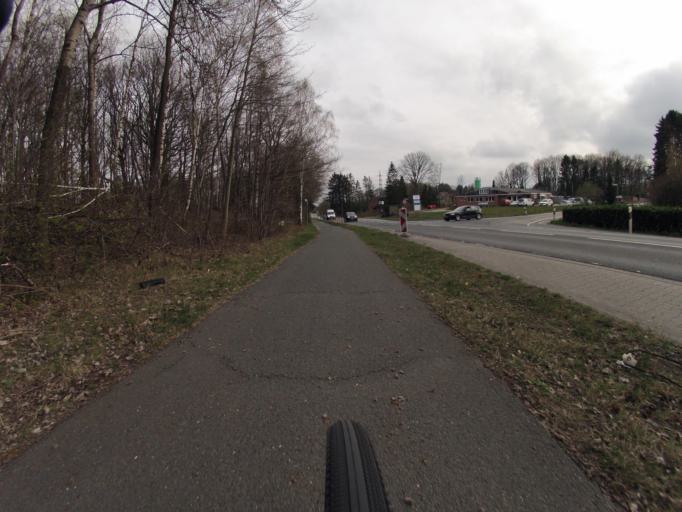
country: DE
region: North Rhine-Westphalia
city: Ibbenburen
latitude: 52.3003
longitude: 7.6922
